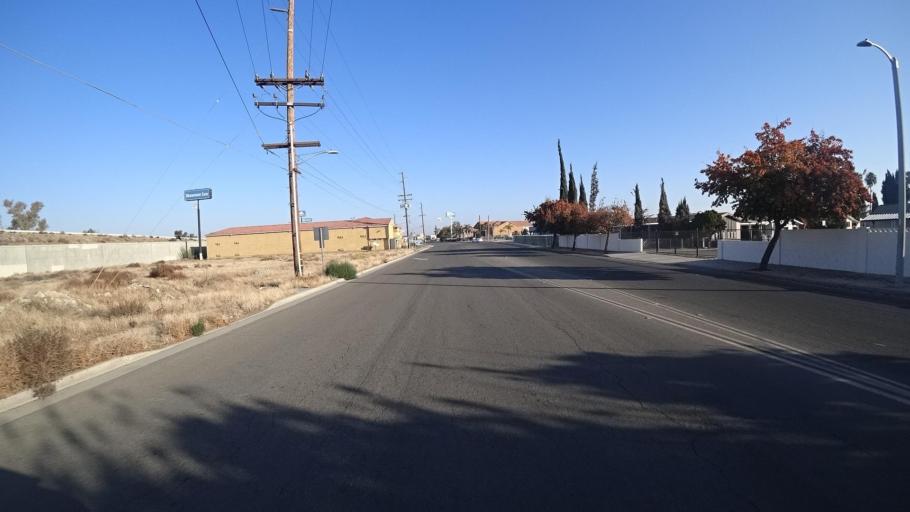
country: US
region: California
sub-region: Kern County
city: Delano
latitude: 35.7861
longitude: -119.2498
